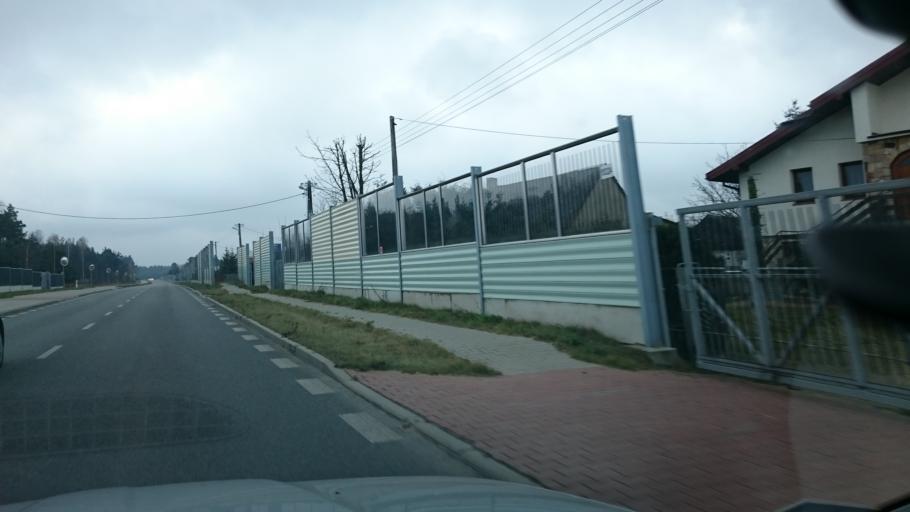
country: PL
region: Swietokrzyskie
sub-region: Powiat konecki
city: Konskie
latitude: 51.1585
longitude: 20.3673
